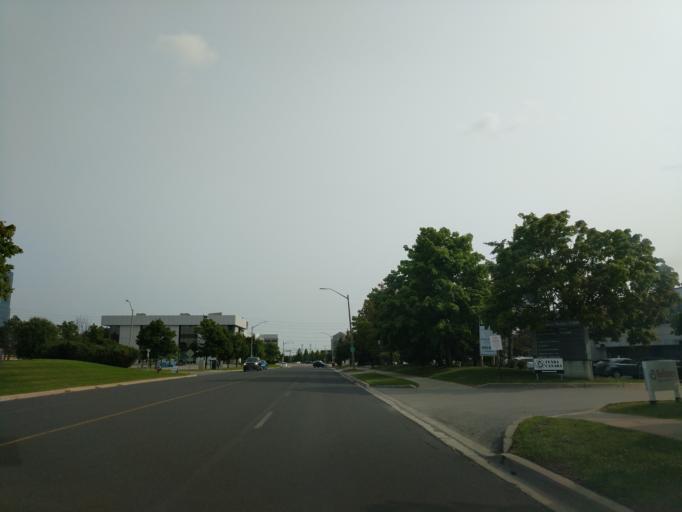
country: CA
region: Ontario
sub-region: York
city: Richmond Hill
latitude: 43.8457
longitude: -79.3873
